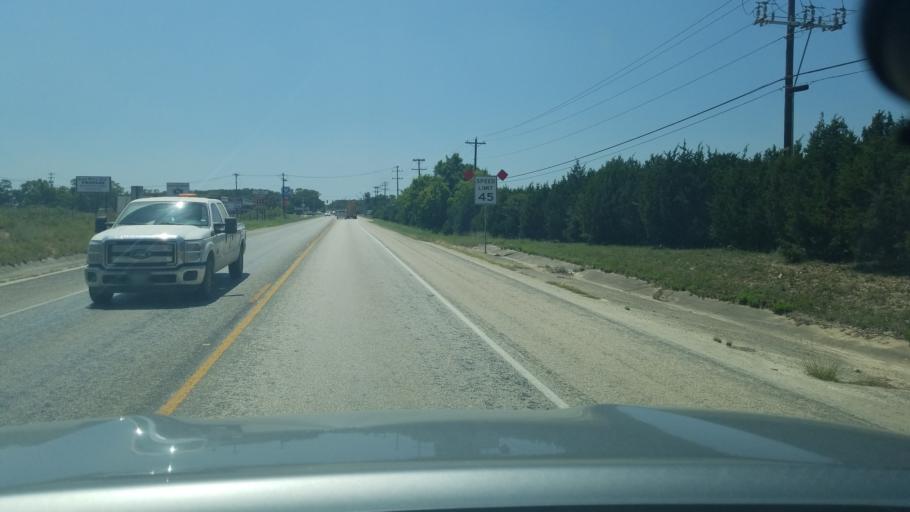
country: US
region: Texas
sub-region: Bexar County
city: Fair Oaks Ranch
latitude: 29.8271
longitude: -98.5692
